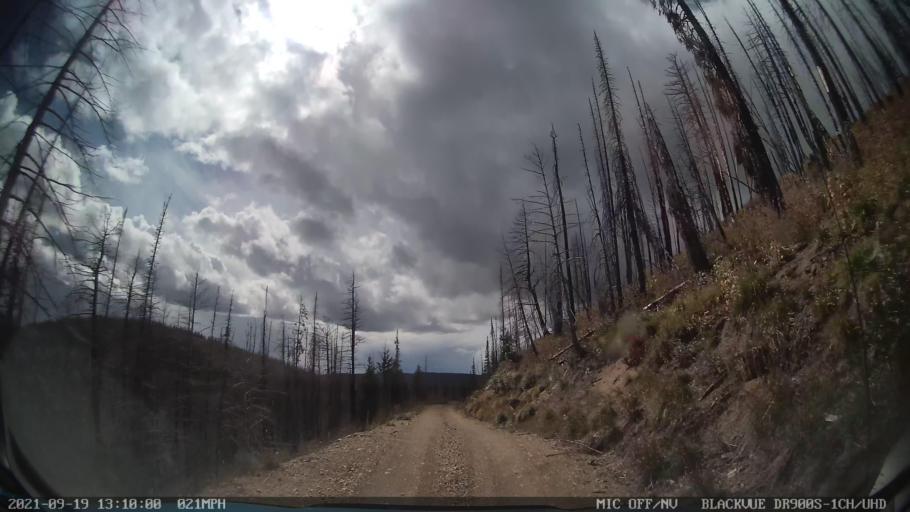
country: US
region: Montana
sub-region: Missoula County
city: Seeley Lake
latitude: 47.1803
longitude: -113.3521
